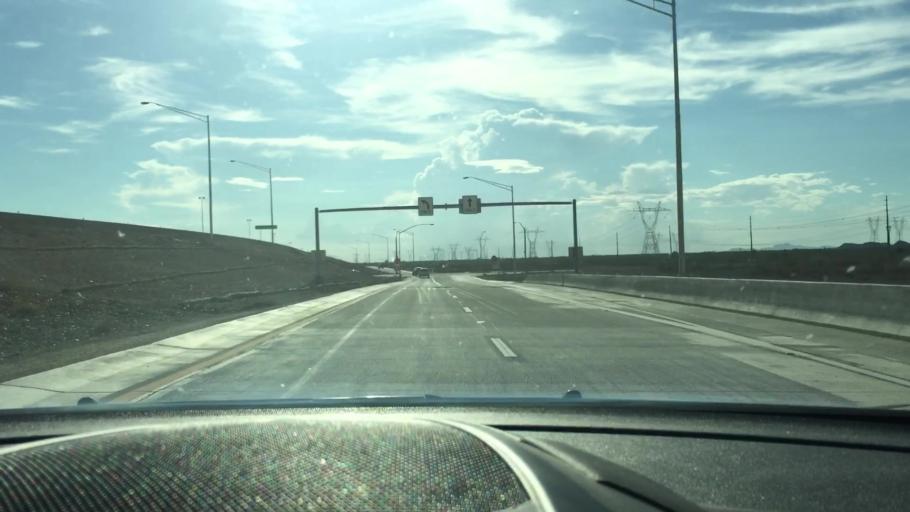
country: US
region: Arizona
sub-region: Maricopa County
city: Sun City West
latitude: 33.6988
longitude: -112.3320
